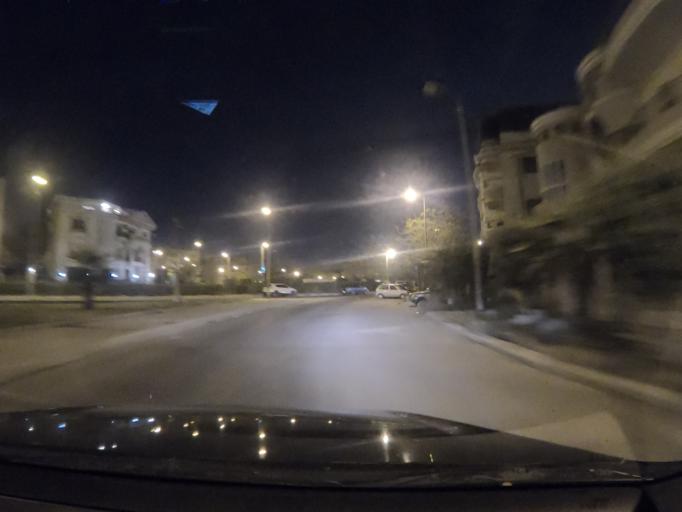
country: EG
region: Muhafazat al Qahirah
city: Cairo
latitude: 30.0105
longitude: 31.4171
